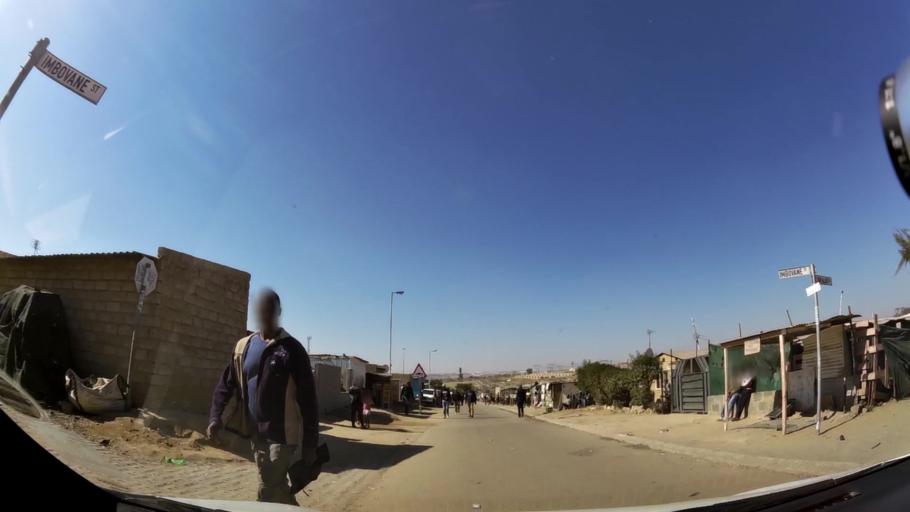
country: ZA
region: Gauteng
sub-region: City of Johannesburg Metropolitan Municipality
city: Midrand
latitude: -25.9175
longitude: 28.0928
